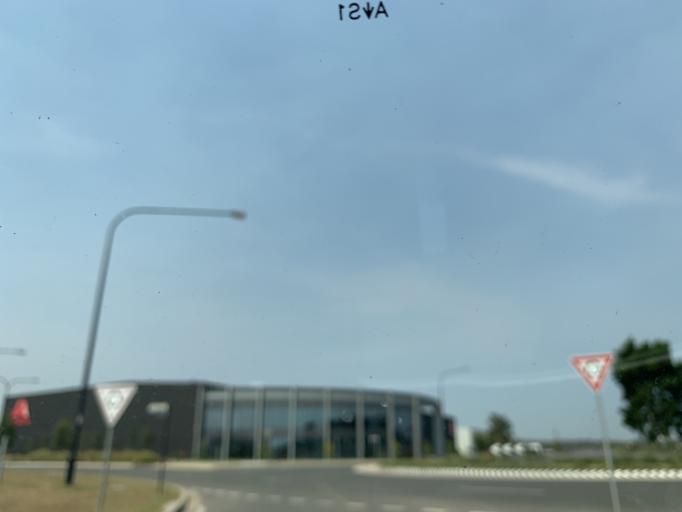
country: AU
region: New South Wales
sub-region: Blacktown
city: Hassall Grove
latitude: -33.7164
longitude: 150.8345
